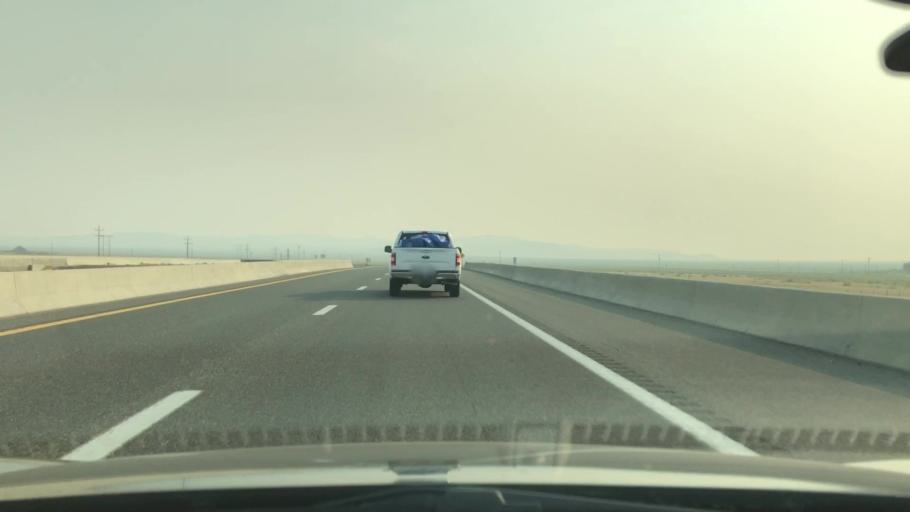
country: US
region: Nevada
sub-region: Pershing County
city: Lovelock
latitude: 40.0600
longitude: -118.6521
